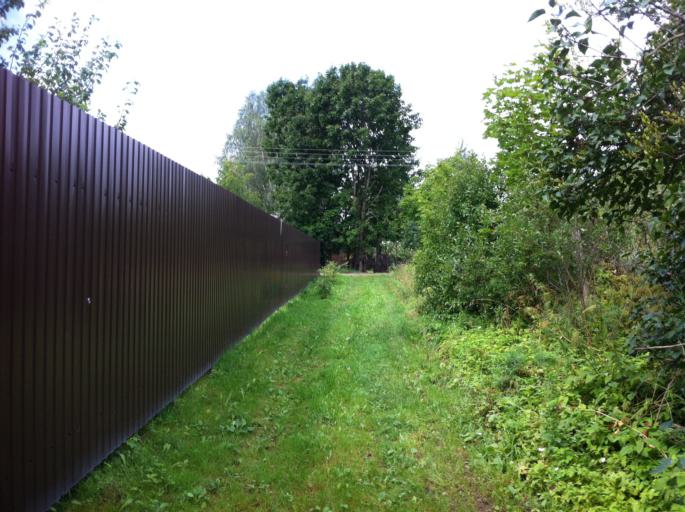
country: RU
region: Pskov
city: Izborsk
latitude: 57.8174
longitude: 27.9581
